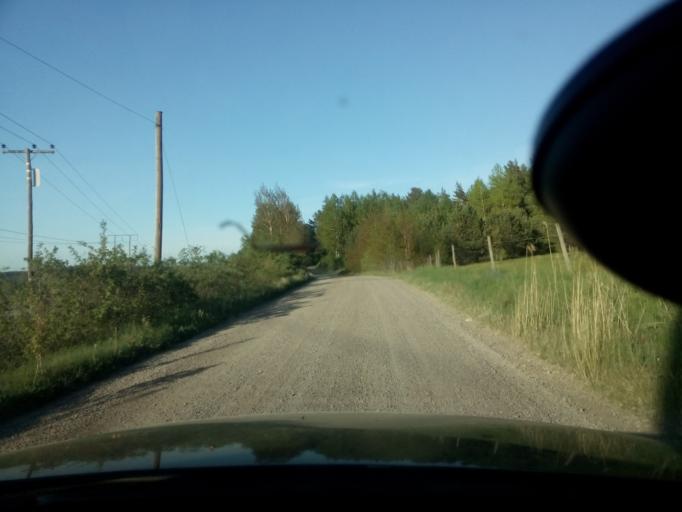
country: SE
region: Soedermanland
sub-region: Nykopings Kommun
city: Nykoping
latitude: 58.7793
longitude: 17.0356
